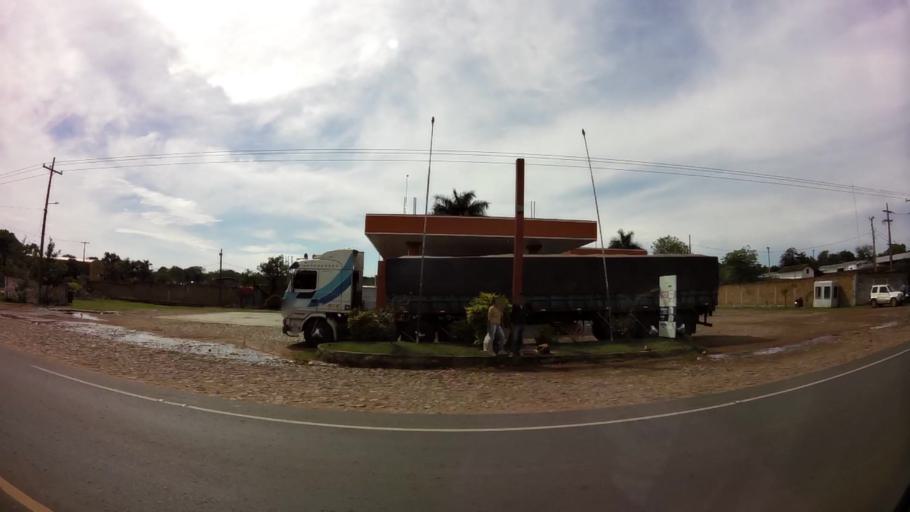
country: PY
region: Central
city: Limpio
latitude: -25.1591
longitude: -57.4746
